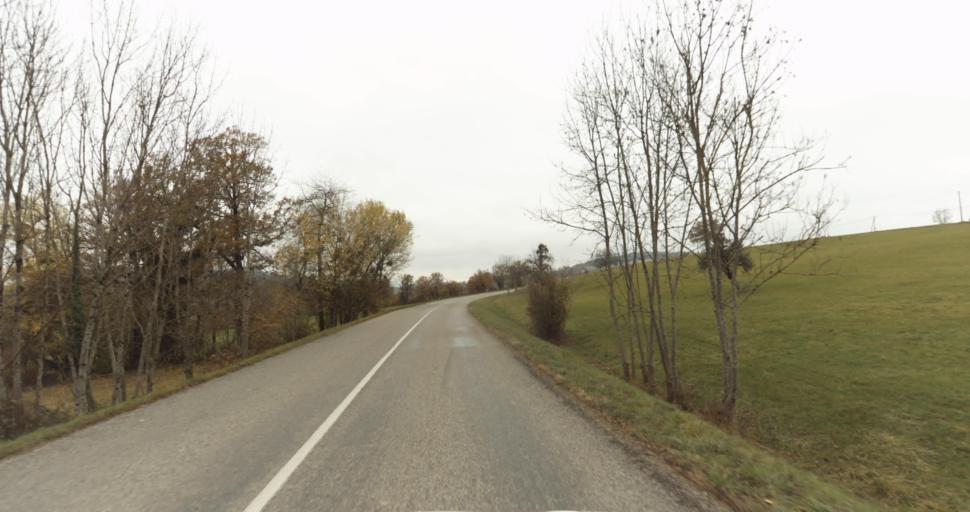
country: FR
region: Rhone-Alpes
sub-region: Departement de la Haute-Savoie
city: Alby-sur-Cheran
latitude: 45.8406
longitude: 6.0405
